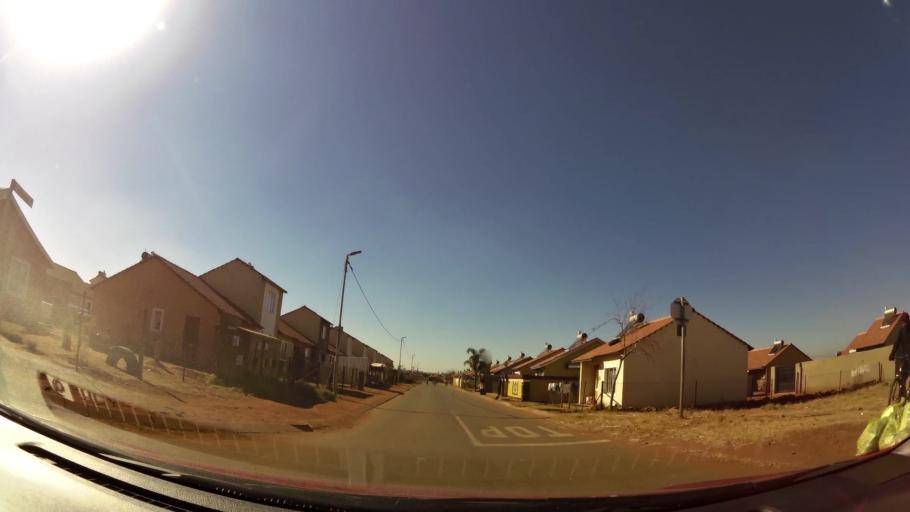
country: ZA
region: Gauteng
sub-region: City of Johannesburg Metropolitan Municipality
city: Soweto
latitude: -26.2366
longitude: 27.8005
